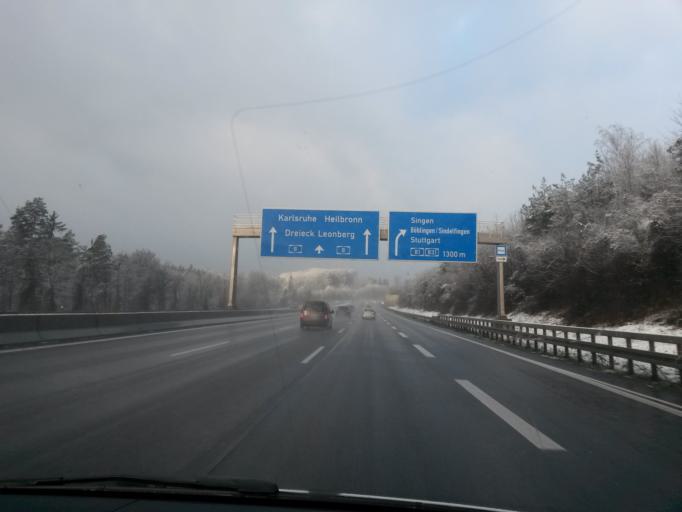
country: DE
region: Baden-Wuerttemberg
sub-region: Regierungsbezirk Stuttgart
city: Steinenbronn
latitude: 48.7136
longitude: 9.0946
